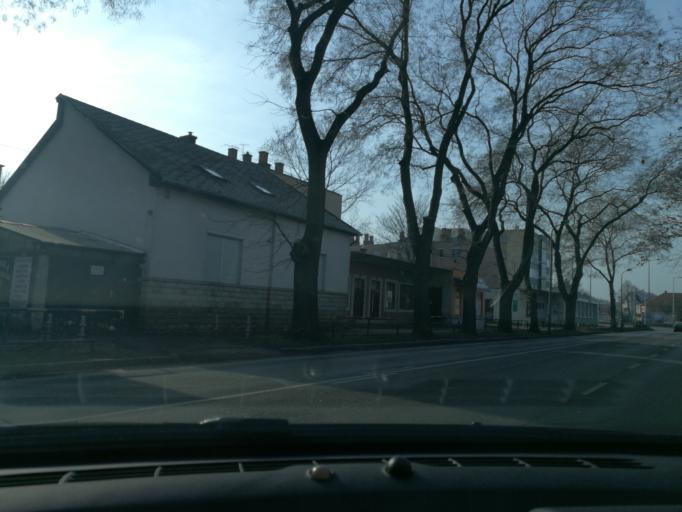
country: HU
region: Szabolcs-Szatmar-Bereg
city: Nyiregyhaza
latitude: 47.9529
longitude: 21.7294
